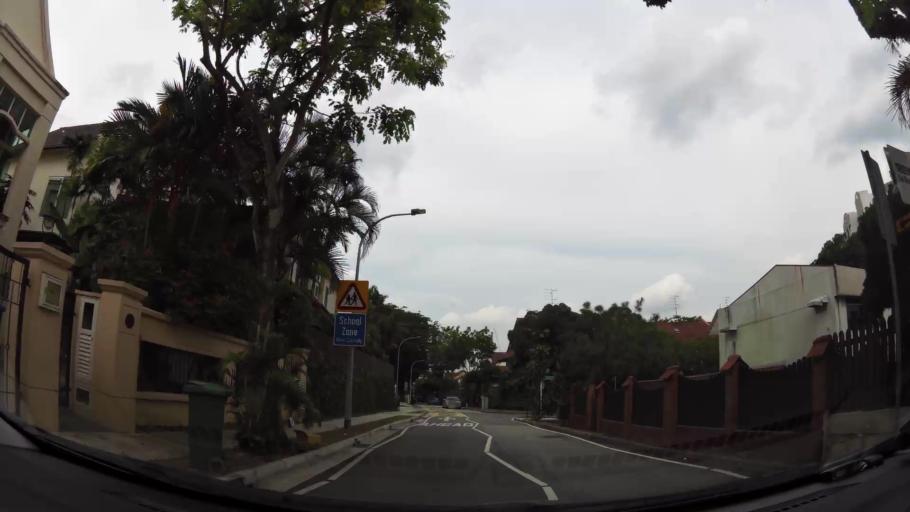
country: SG
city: Singapore
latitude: 1.3197
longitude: 103.8077
